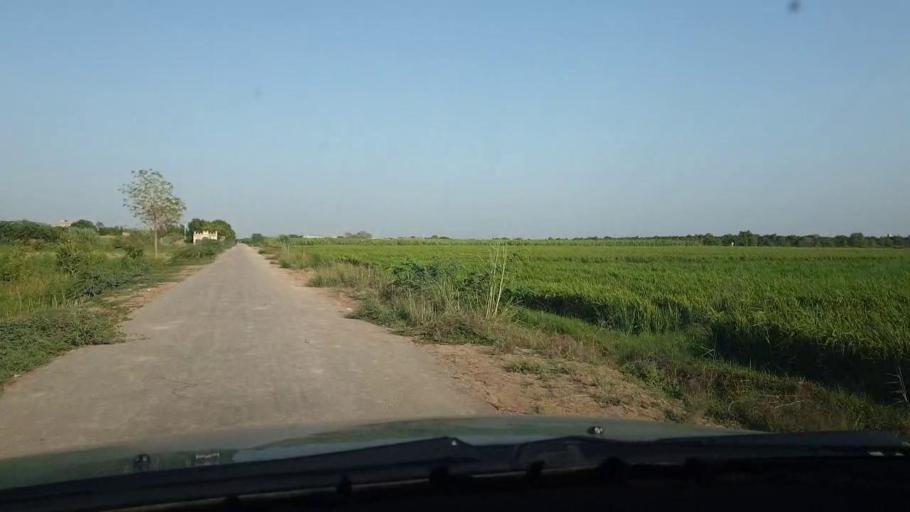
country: PK
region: Sindh
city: Mirwah Gorchani
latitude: 25.2997
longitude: 68.9647
